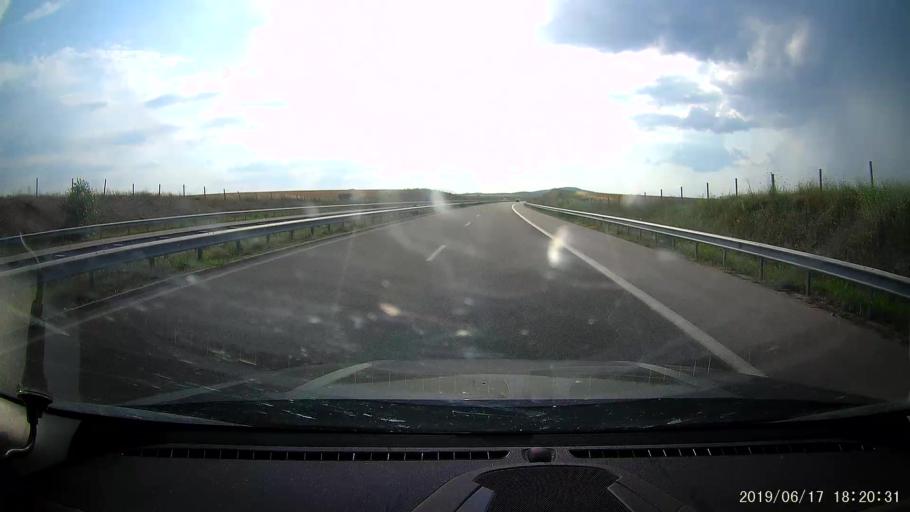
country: BG
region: Khaskovo
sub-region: Obshtina Simeonovgrad
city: Simeonovgrad
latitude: 41.9621
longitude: 25.8108
